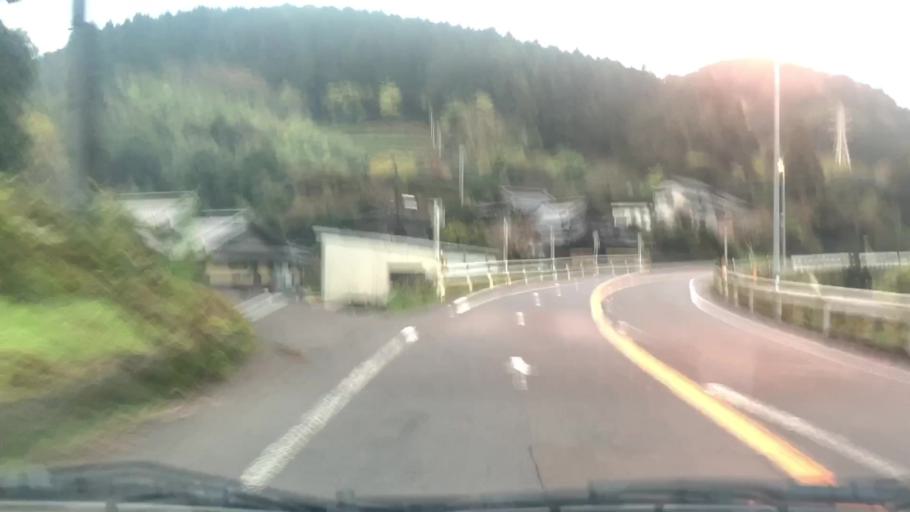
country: JP
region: Saga Prefecture
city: Ureshinomachi-shimojuku
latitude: 33.0681
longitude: 129.9635
